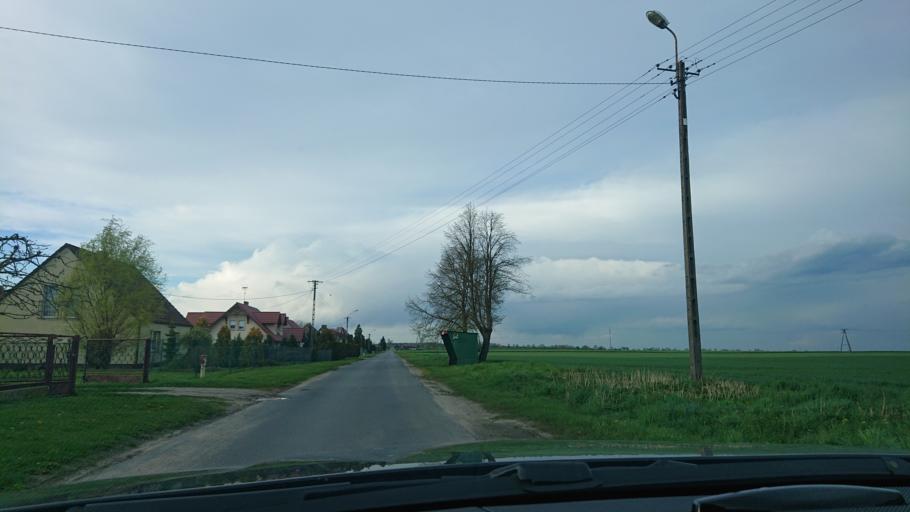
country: PL
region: Greater Poland Voivodeship
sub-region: Powiat gnieznienski
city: Lubowo
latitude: 52.5718
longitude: 17.4753
